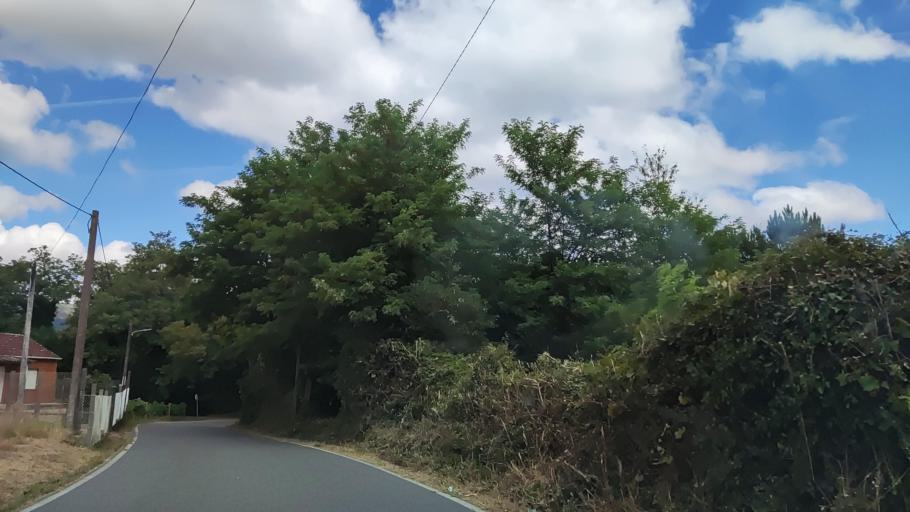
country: ES
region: Galicia
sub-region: Provincia da Coruna
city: Rois
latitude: 42.7816
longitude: -8.6682
